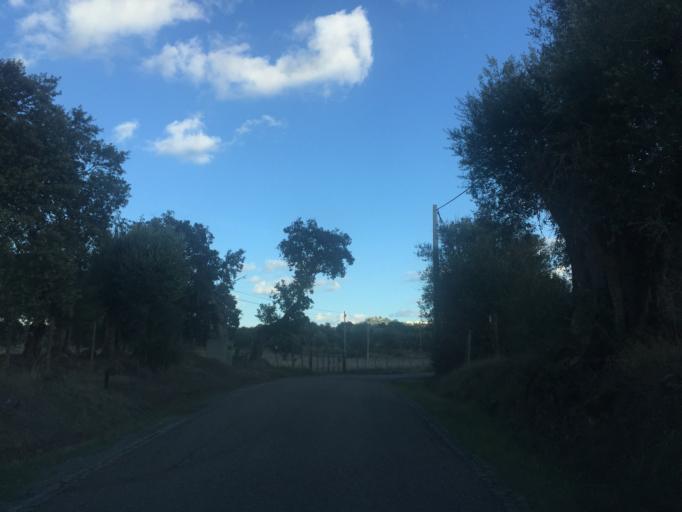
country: PT
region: Portalegre
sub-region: Alter do Chao
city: Alter do Chao
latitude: 39.1917
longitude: -7.6466
